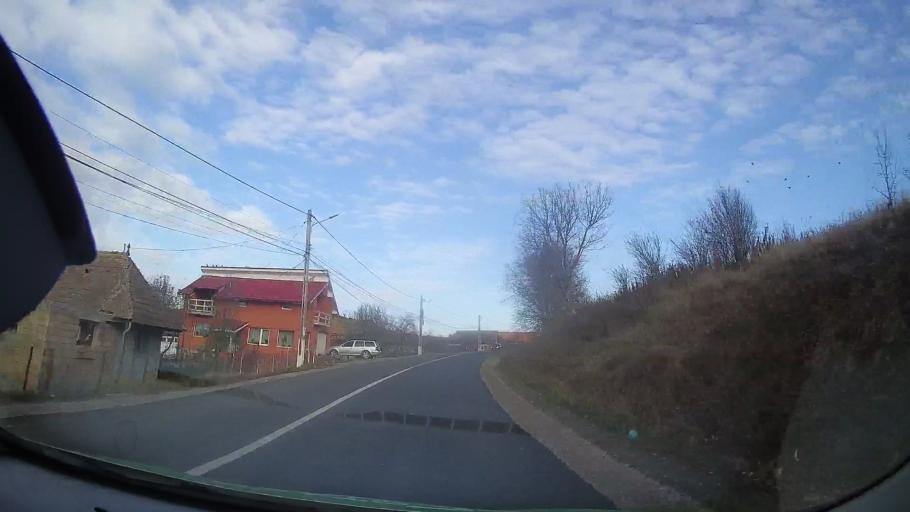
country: RO
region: Mures
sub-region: Comuna Iclanzel
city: Iclanzel
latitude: 46.5208
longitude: 24.2729
